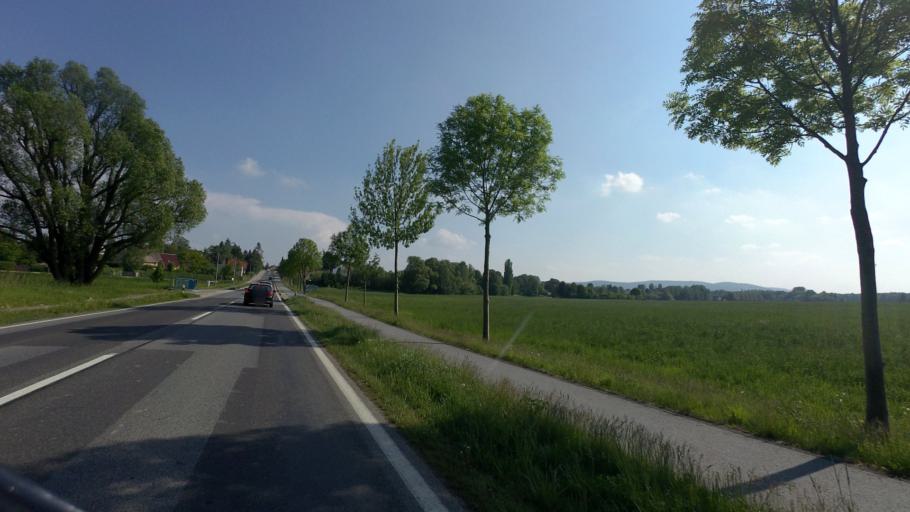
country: DE
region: Saxony
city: Bautzen
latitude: 51.1602
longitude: 14.4300
